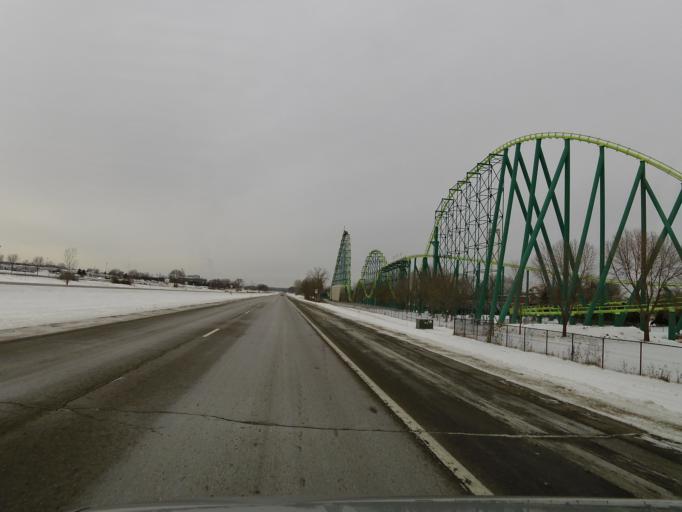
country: US
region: Minnesota
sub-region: Hennepin County
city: Eden Prairie
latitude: 44.7967
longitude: -93.4521
